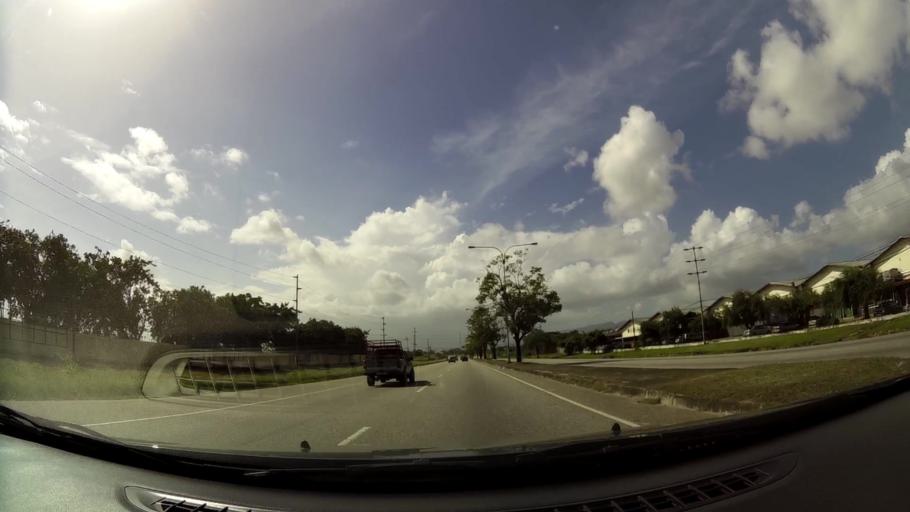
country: TT
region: Borough of Arima
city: Arima
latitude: 10.6112
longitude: -61.2962
